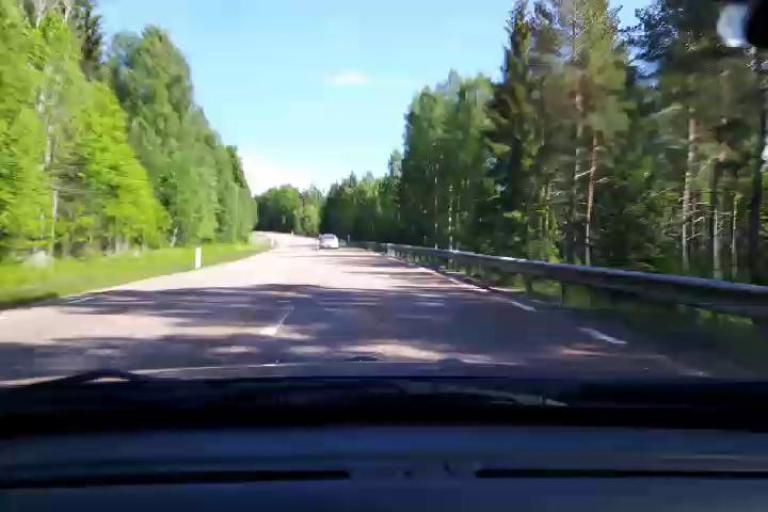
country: SE
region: Gaevleborg
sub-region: Hudiksvalls Kommun
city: Delsbo
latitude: 61.7643
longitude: 16.7185
